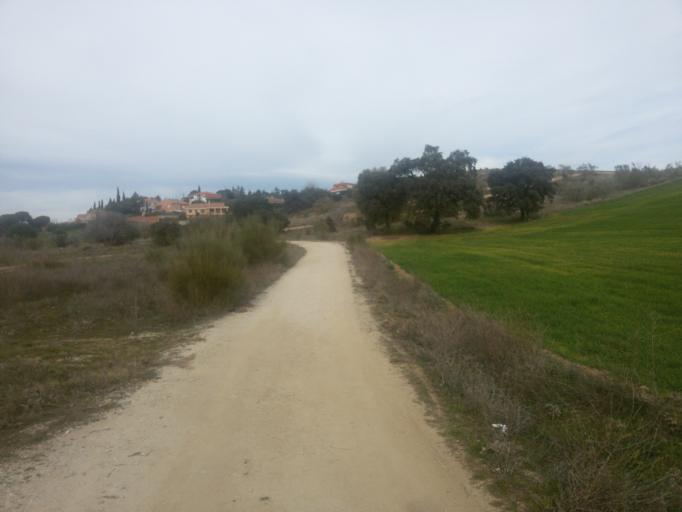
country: ES
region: Madrid
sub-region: Provincia de Madrid
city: Sevilla La Nueva
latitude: 40.3385
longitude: -4.0284
